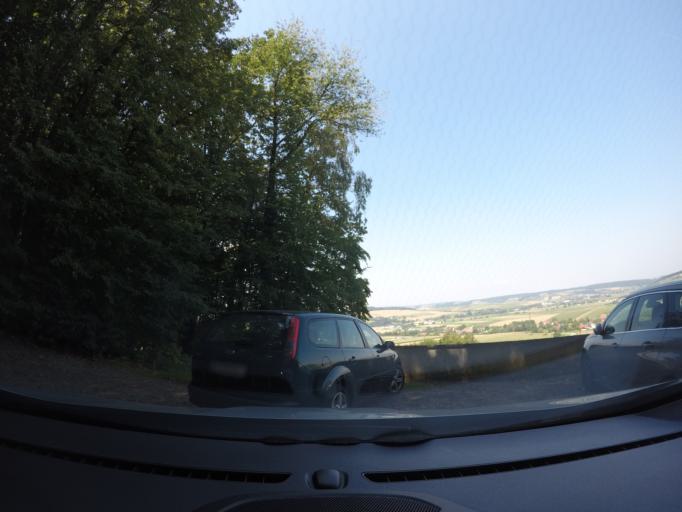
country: AT
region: Lower Austria
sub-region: Politischer Bezirk Sankt Polten
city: Maria-Anzbach
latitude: 48.2148
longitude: 15.9315
